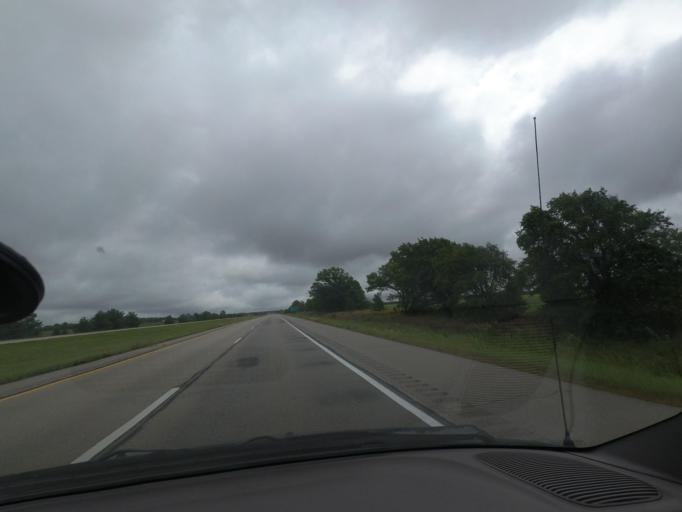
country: US
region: Illinois
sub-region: Piatt County
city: Monticello
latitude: 40.0306
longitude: -88.6401
